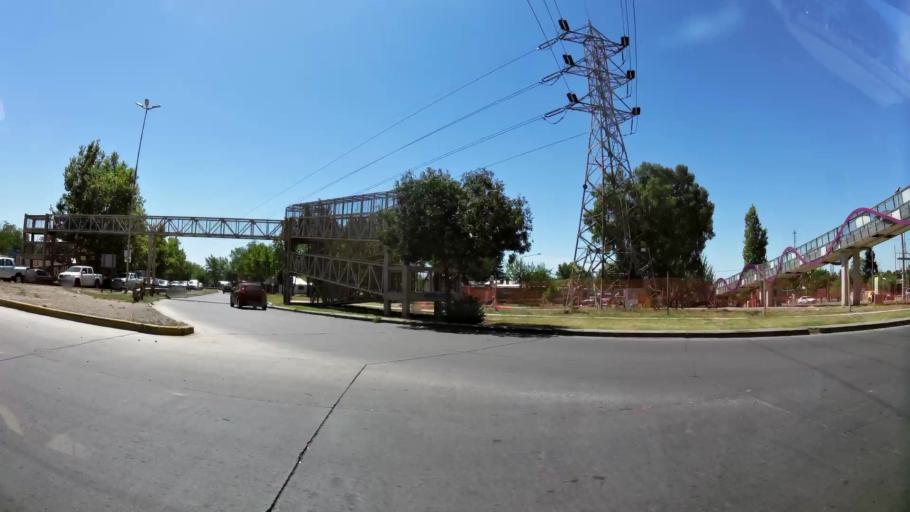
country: AR
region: Mendoza
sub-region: Departamento de Godoy Cruz
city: Godoy Cruz
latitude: -32.9235
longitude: -68.8638
